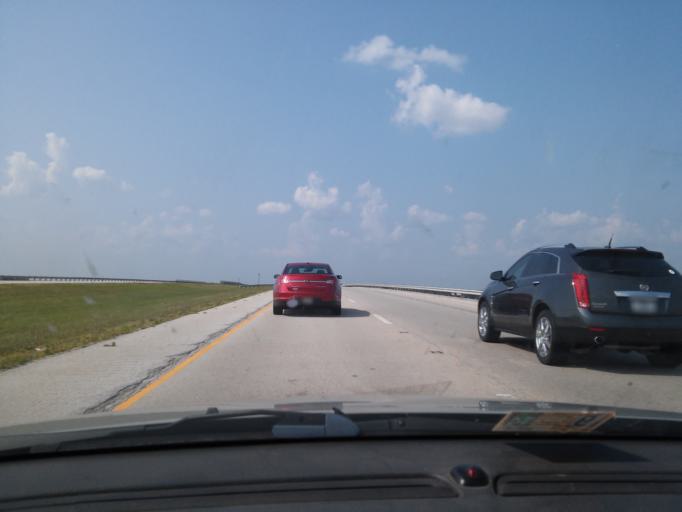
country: US
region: Illinois
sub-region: Livingston County
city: Pontiac
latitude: 40.8789
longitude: -88.6713
